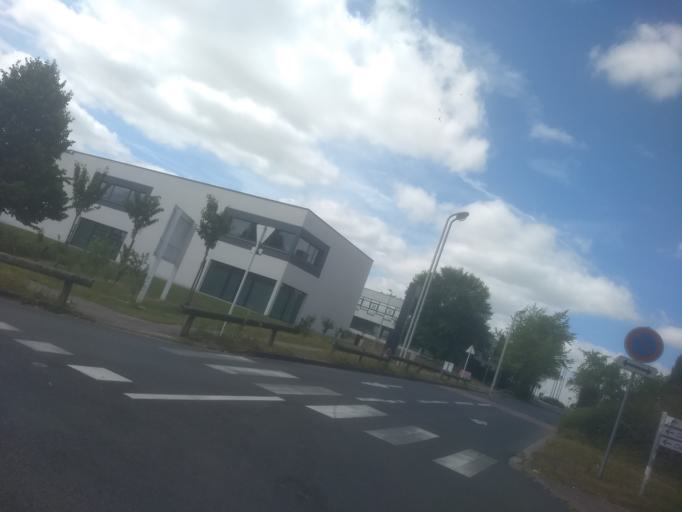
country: FR
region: Nord-Pas-de-Calais
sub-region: Departement du Pas-de-Calais
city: Anzin-Saint-Aubin
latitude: 50.3024
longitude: 2.7337
